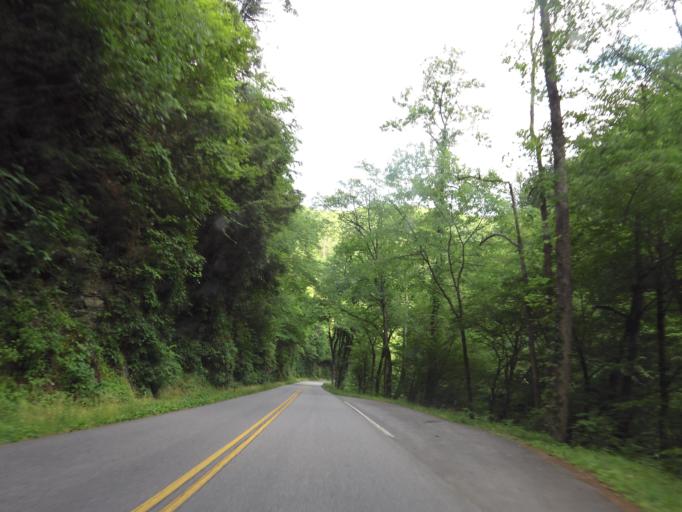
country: US
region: Tennessee
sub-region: Sevier County
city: Pigeon Forge
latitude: 35.6671
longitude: -83.6994
